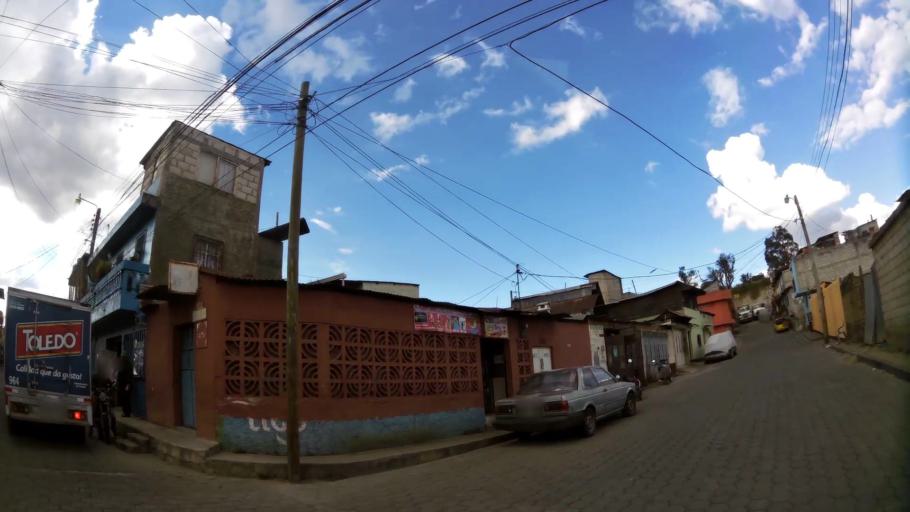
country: GT
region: Quetzaltenango
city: Quetzaltenango
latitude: 14.8516
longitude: -91.5191
